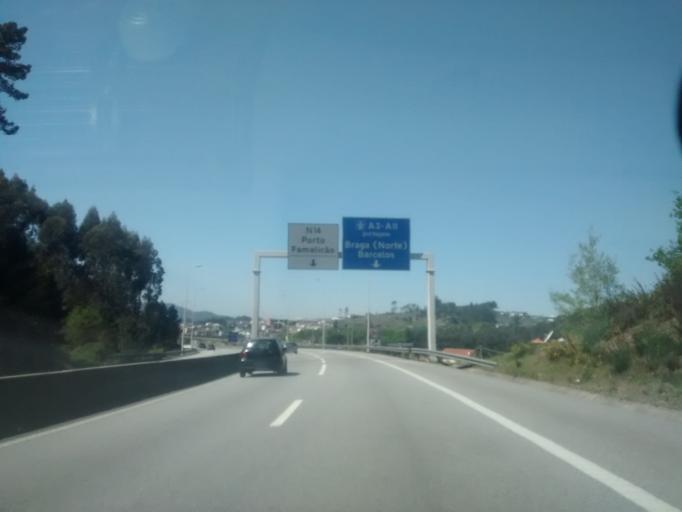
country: PT
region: Braga
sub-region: Braga
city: Braga
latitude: 41.5195
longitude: -8.4387
